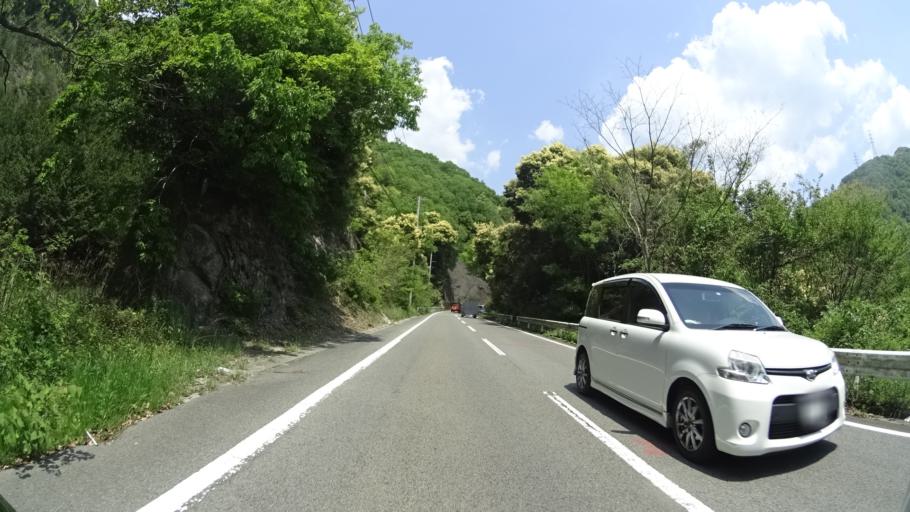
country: JP
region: Ehime
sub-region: Shikoku-chuo Shi
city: Matsuyama
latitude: 33.8749
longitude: 132.8324
